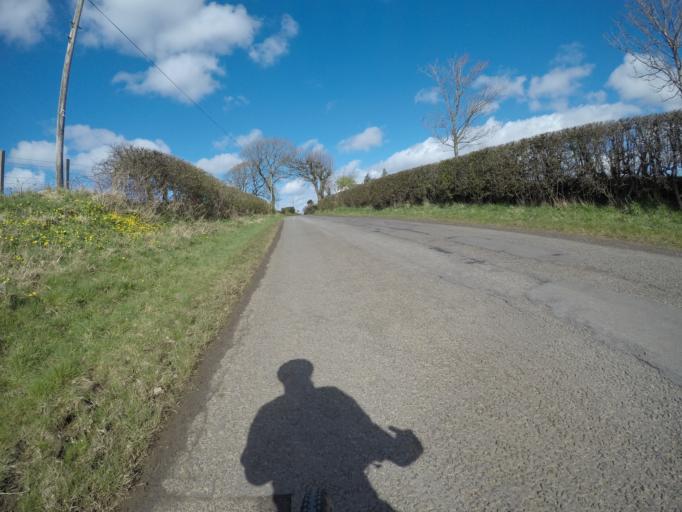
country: GB
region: Scotland
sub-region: East Ayrshire
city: Crosshouse
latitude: 55.6057
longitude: -4.5745
